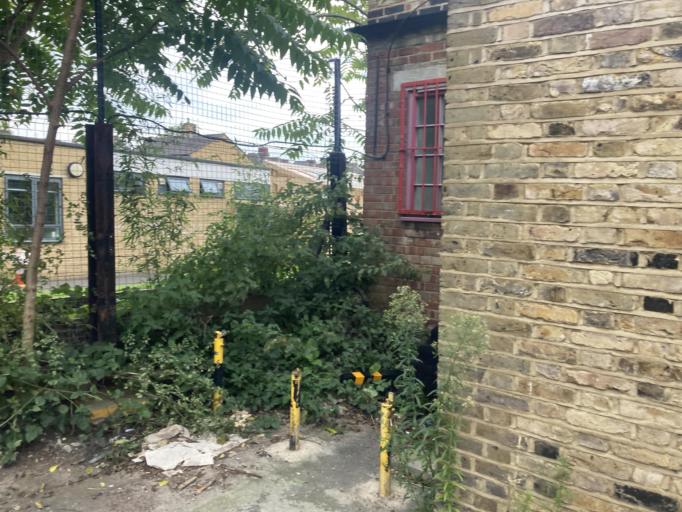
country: GB
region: England
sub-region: Greater London
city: Crouch End
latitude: 51.5669
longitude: -0.1145
